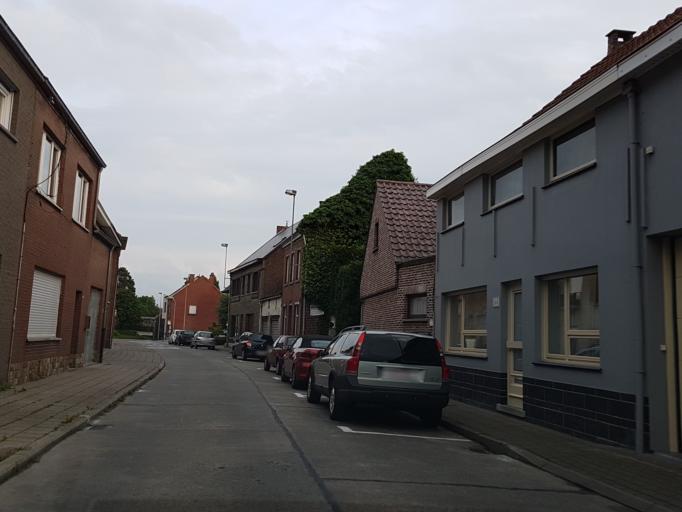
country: BE
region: Flanders
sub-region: Provincie Oost-Vlaanderen
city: Denderleeuw
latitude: 50.9163
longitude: 4.0707
